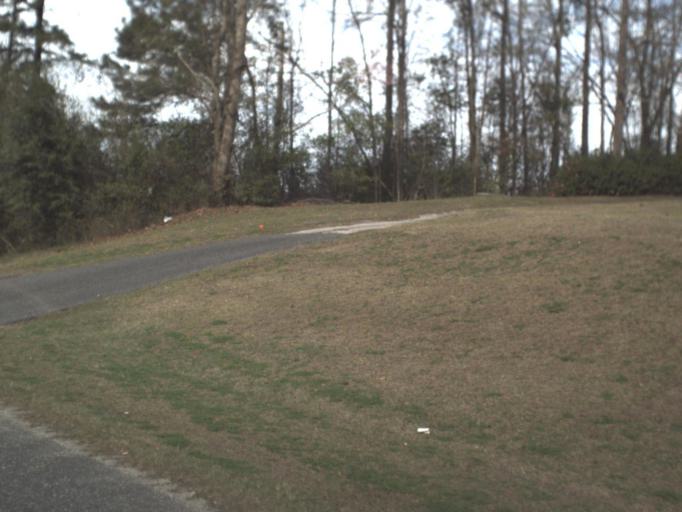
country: US
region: Florida
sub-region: Jefferson County
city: Monticello
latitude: 30.5646
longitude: -83.8699
